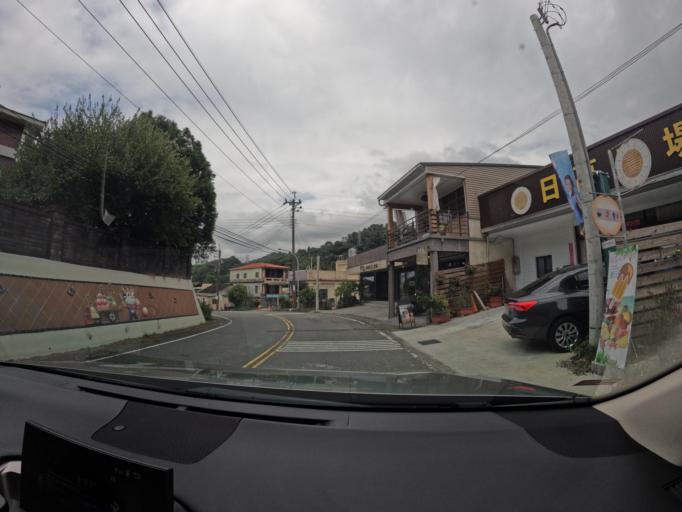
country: TW
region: Taiwan
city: Fengyuan
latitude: 24.3343
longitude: 120.8750
